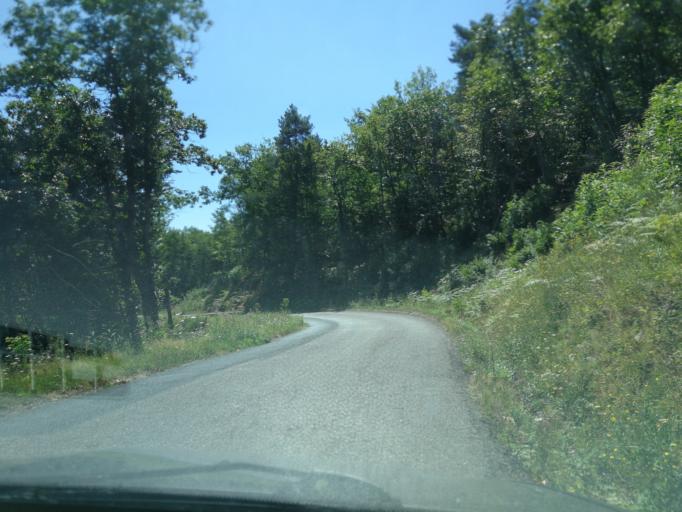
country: FR
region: Limousin
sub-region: Departement de la Correze
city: Argentat
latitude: 45.0961
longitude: 1.8940
